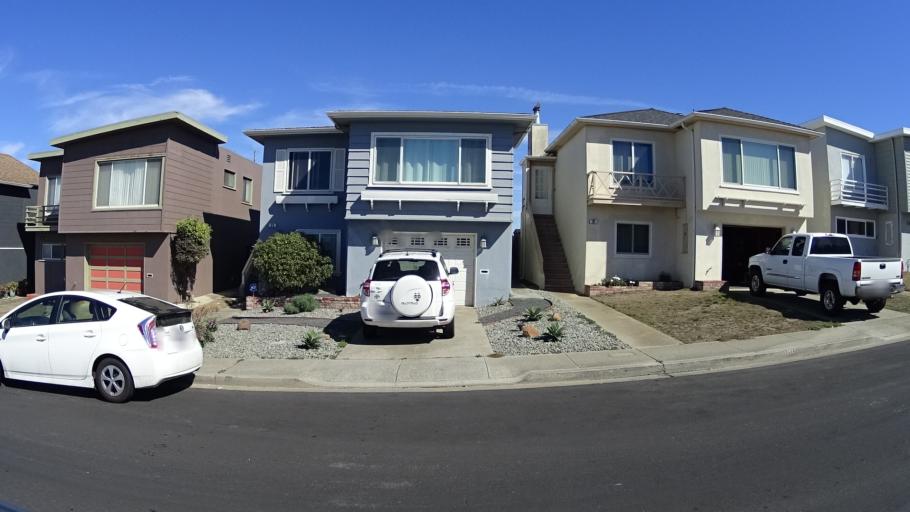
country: US
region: California
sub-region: San Mateo County
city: Broadmoor
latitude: 37.6938
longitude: -122.4958
